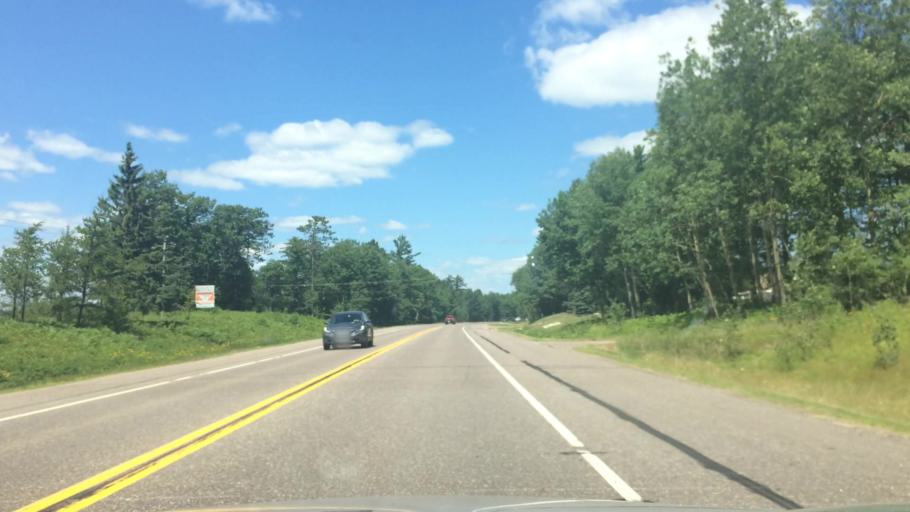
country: US
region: Wisconsin
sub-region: Vilas County
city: Lac du Flambeau
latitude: 45.9455
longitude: -89.6988
